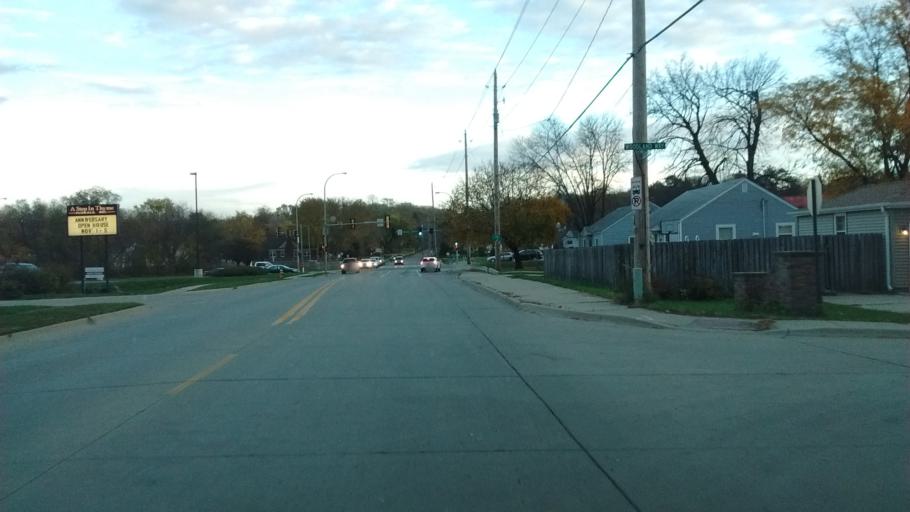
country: US
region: Iowa
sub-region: Woodbury County
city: Sioux City
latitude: 42.5262
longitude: -96.4164
